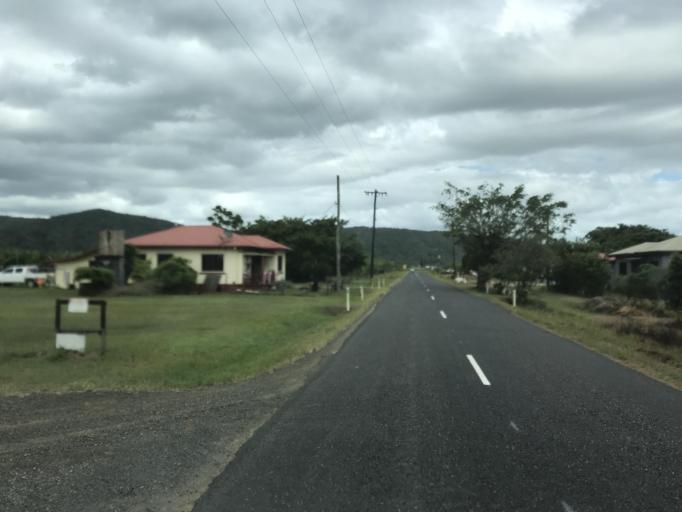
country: AU
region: Queensland
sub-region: Cassowary Coast
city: Innisfail
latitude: -17.6208
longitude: 146.0220
